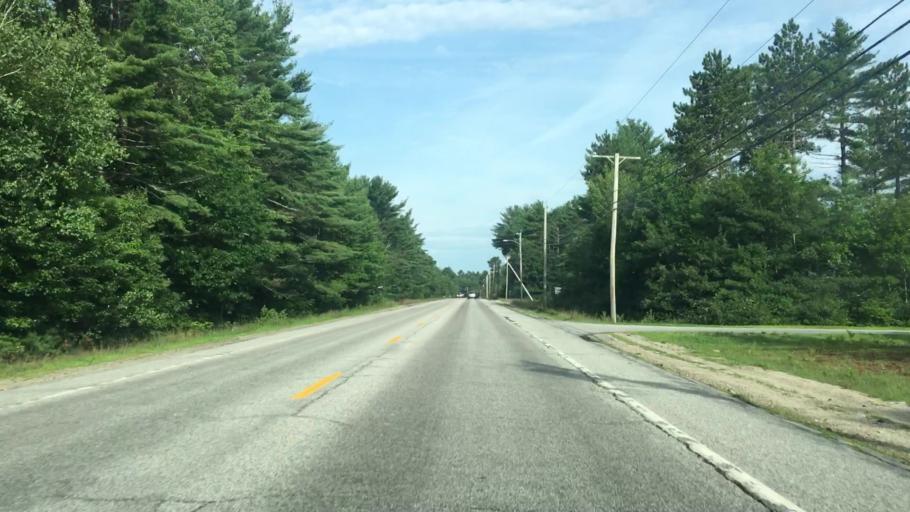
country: US
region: Maine
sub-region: Cumberland County
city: Steep Falls
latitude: 43.7344
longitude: -70.6195
